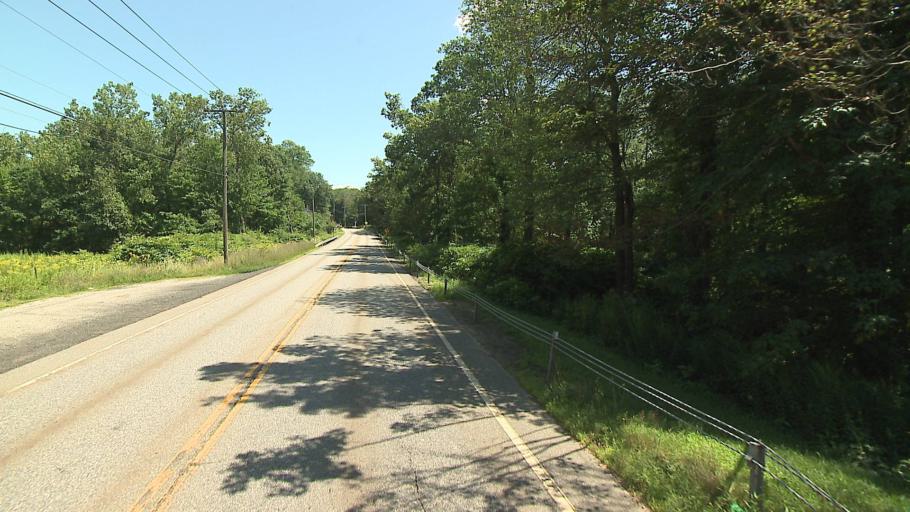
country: US
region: Connecticut
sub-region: Litchfield County
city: Northwest Harwinton
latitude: 41.7771
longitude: -73.0009
